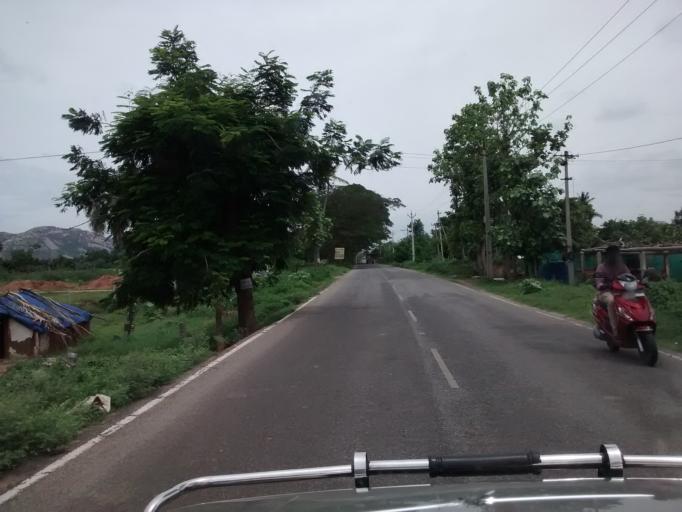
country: IN
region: Andhra Pradesh
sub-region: Chittoor
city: Narasingapuram
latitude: 13.6107
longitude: 79.3367
